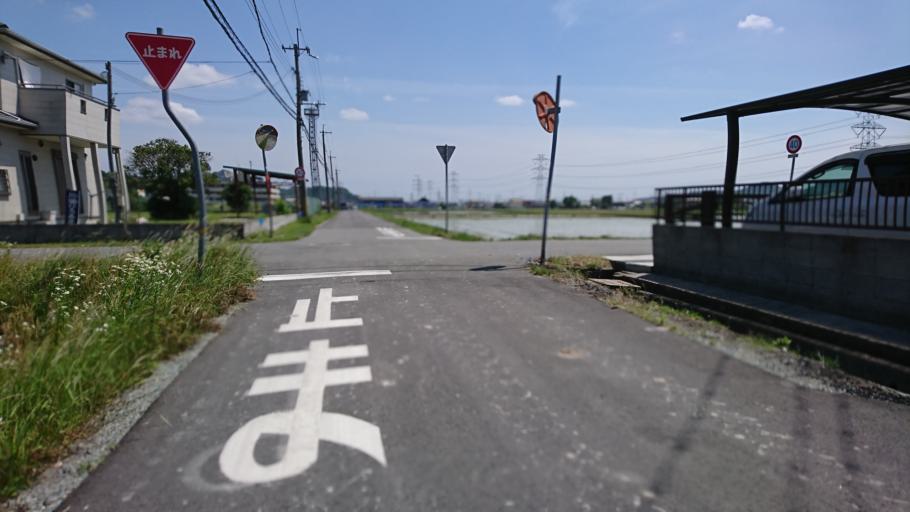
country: JP
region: Hyogo
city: Kakogawacho-honmachi
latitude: 34.8012
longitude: 134.7858
